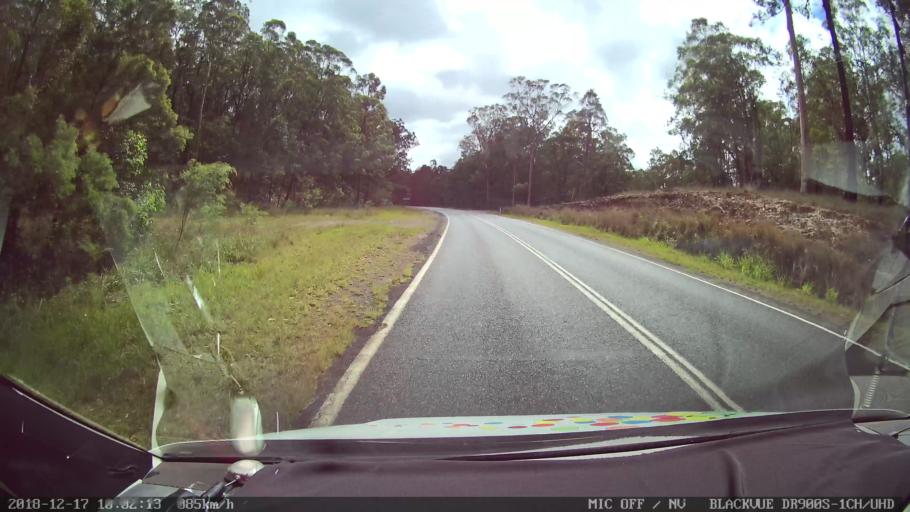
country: AU
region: New South Wales
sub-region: Tenterfield Municipality
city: Carrolls Creek
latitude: -28.9037
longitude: 152.4489
